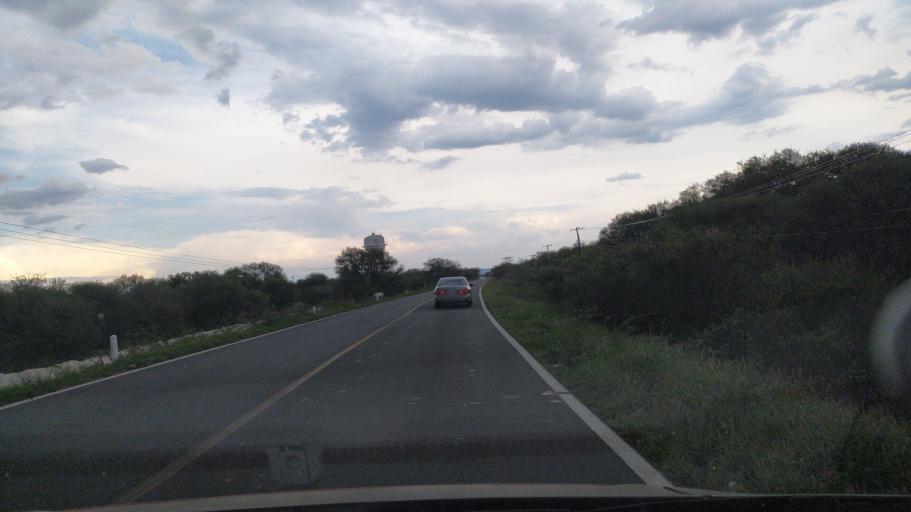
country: MX
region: Guanajuato
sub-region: San Francisco del Rincon
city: San Ignacio de Hidalgo
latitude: 20.8191
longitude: -101.9026
